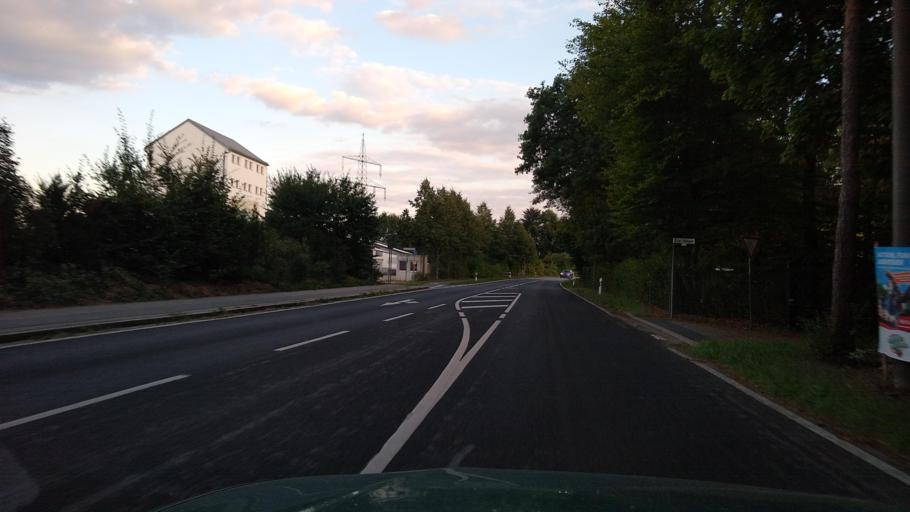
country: DE
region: Bavaria
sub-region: Regierungsbezirk Mittelfranken
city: Altdorf
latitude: 49.3995
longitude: 11.3497
